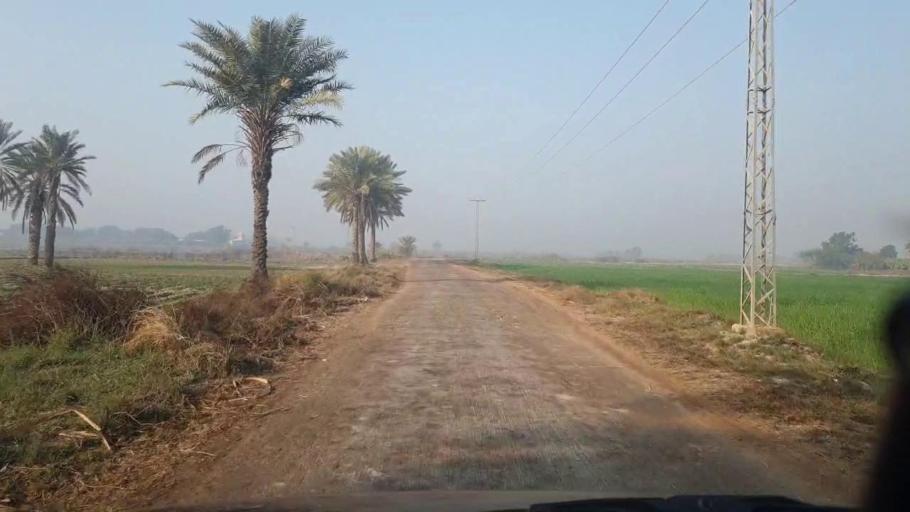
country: PK
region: Sindh
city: Shahdadpur
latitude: 25.8507
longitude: 68.6405
